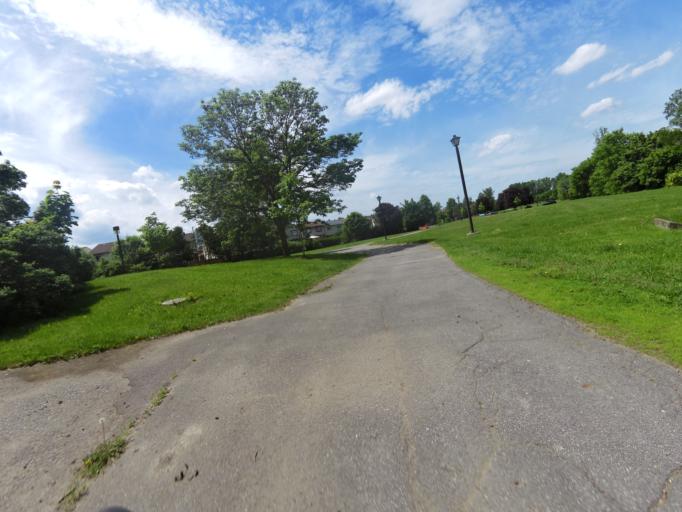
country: CA
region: Ontario
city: Ottawa
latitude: 45.3628
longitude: -75.6402
